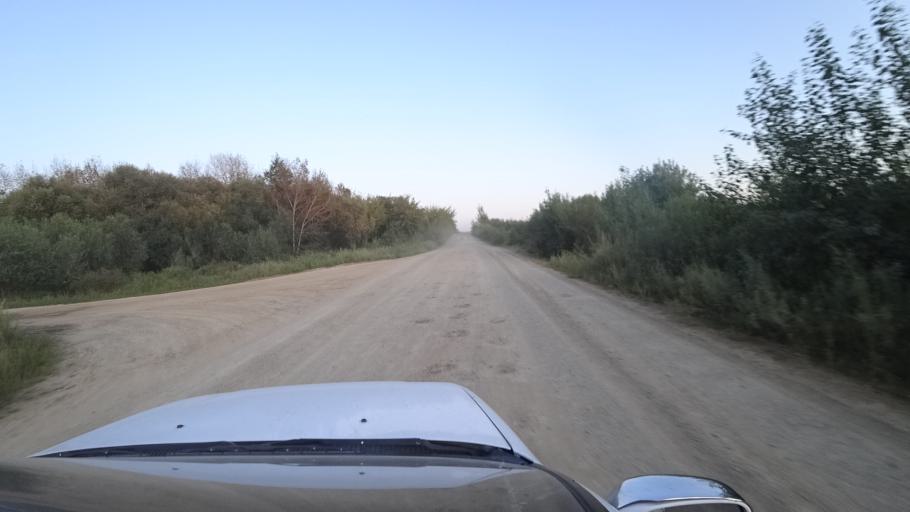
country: RU
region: Primorskiy
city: Dal'nerechensk
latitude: 45.9432
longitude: 133.7599
